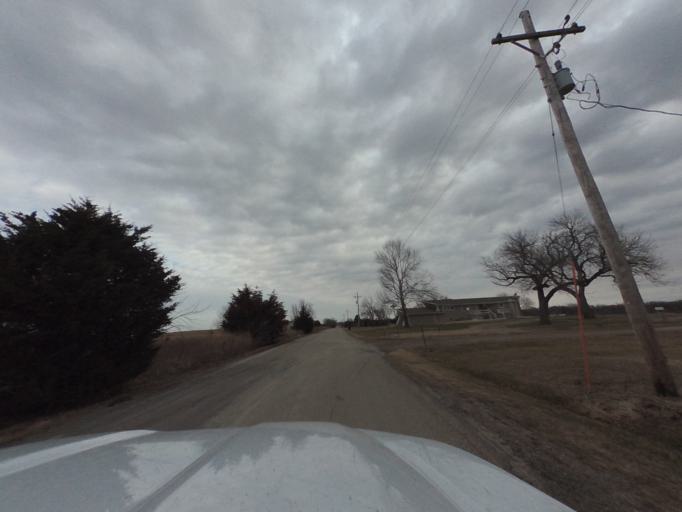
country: US
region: Kansas
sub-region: Chase County
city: Cottonwood Falls
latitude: 38.4247
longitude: -96.3733
